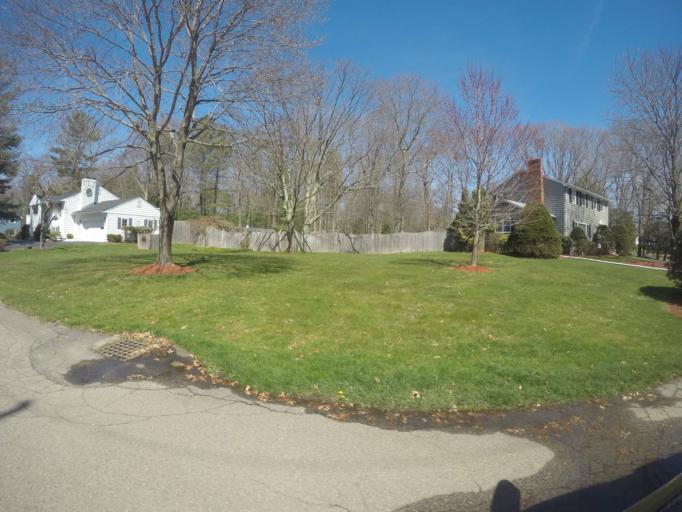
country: US
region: Massachusetts
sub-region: Bristol County
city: Easton
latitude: 42.0374
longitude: -71.0894
